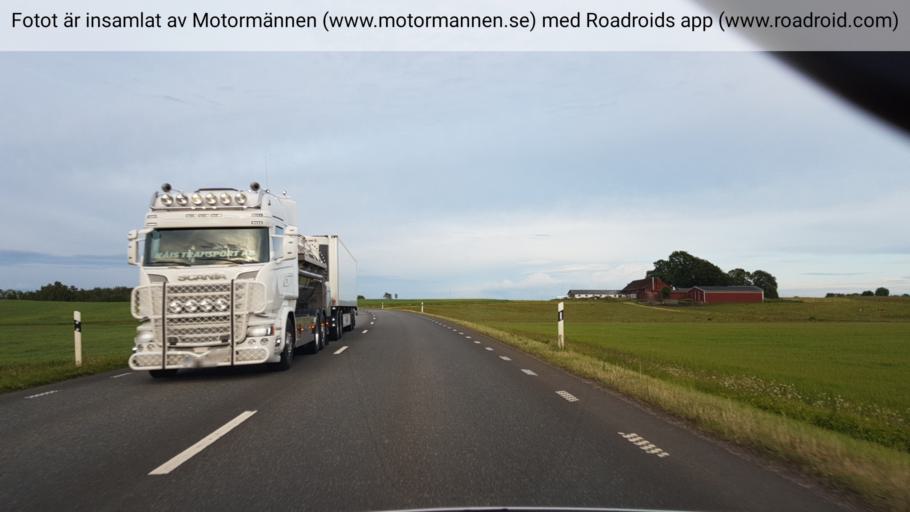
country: SE
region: Vaestra Goetaland
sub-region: Falkopings Kommun
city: Falkoeping
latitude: 58.1804
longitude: 13.5786
